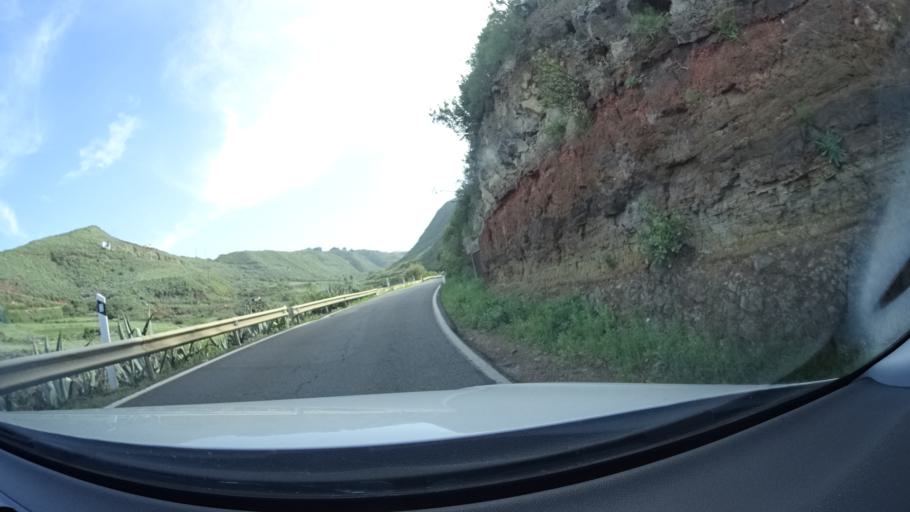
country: ES
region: Canary Islands
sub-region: Provincia de Las Palmas
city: Guia
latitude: 28.1120
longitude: -15.6413
